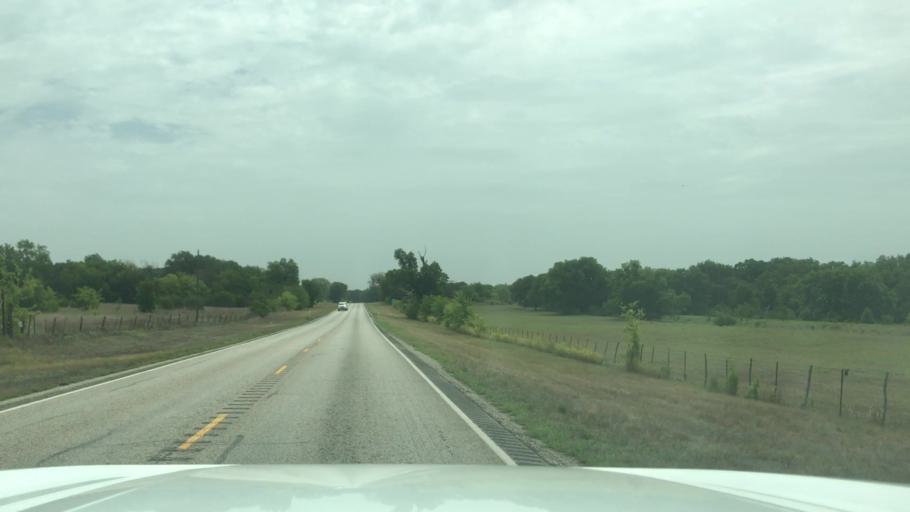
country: US
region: Texas
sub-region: Hamilton County
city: Hico
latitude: 32.0415
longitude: -98.1303
